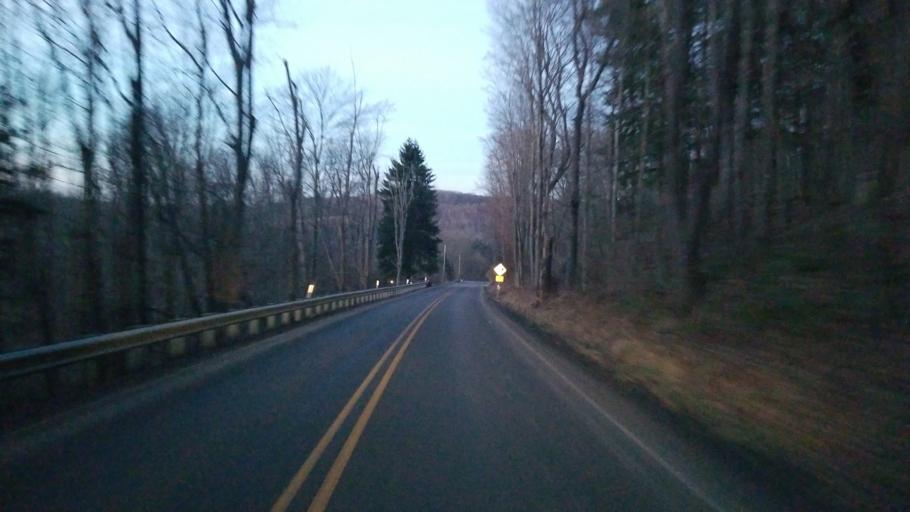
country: US
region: Pennsylvania
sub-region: Jefferson County
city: Punxsutawney
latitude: 40.8643
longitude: -79.1730
